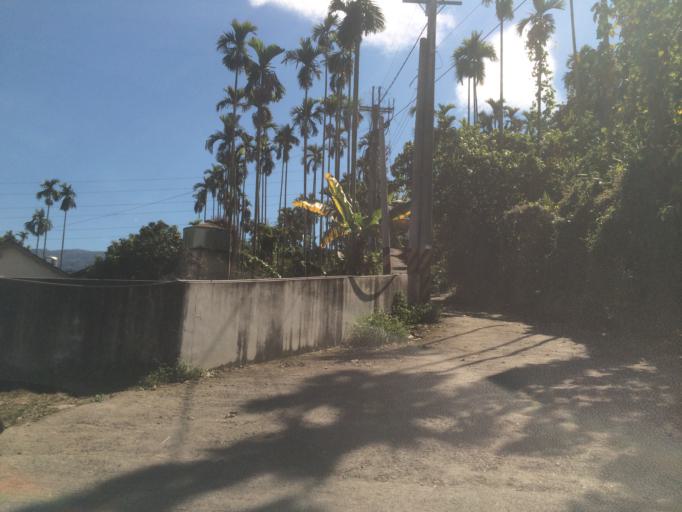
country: TW
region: Taiwan
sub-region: Yunlin
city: Douliu
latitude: 23.6909
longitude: 120.6202
